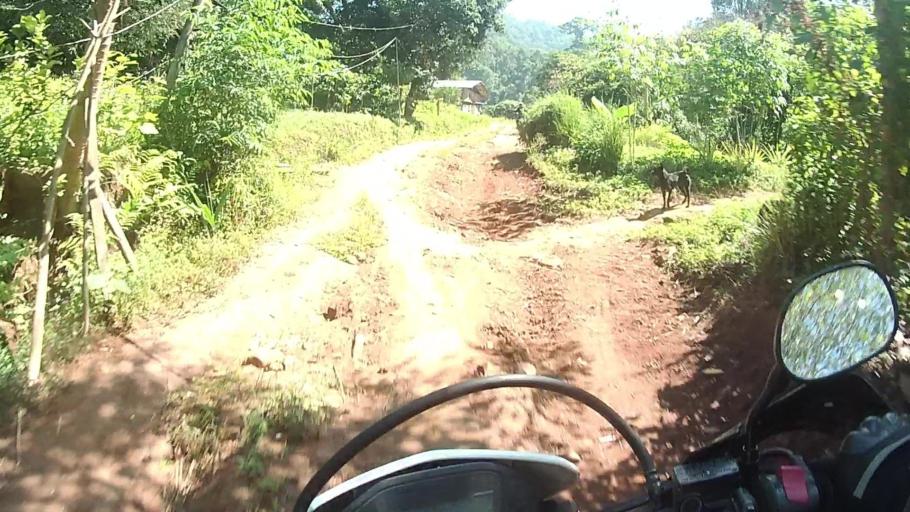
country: TH
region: Chiang Mai
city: Phrao
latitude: 19.4965
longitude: 99.2839
